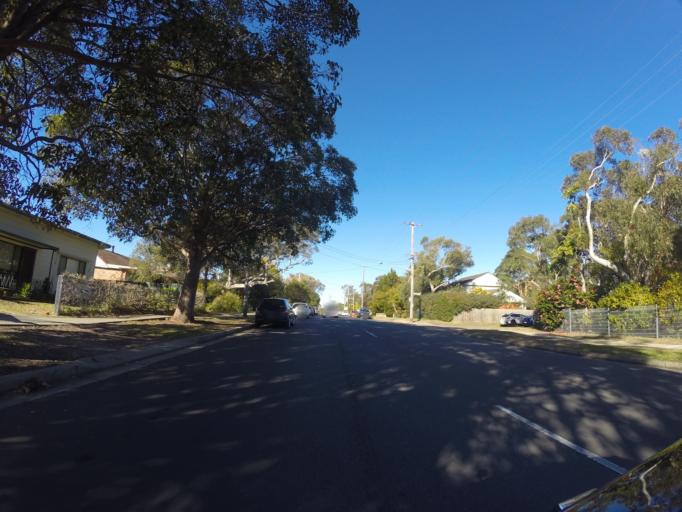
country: AU
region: New South Wales
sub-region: Sutherland Shire
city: Engadine
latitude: -34.0566
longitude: 151.0036
